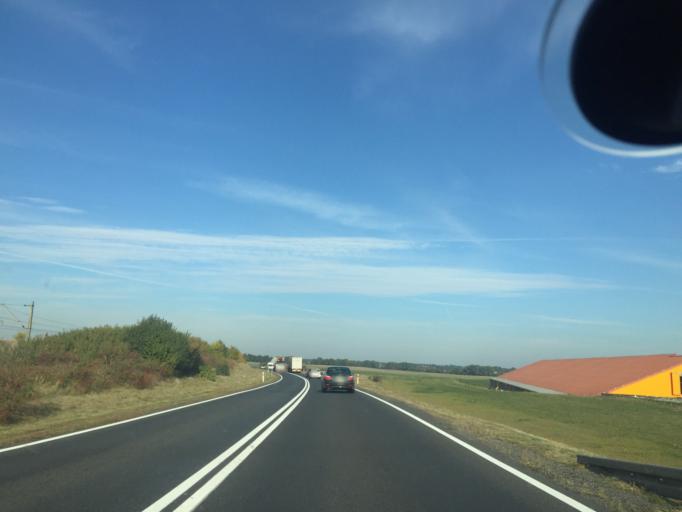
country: PL
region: Greater Poland Voivodeship
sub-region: Powiat gnieznienski
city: Trzemeszno
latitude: 52.5879
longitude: 17.8869
